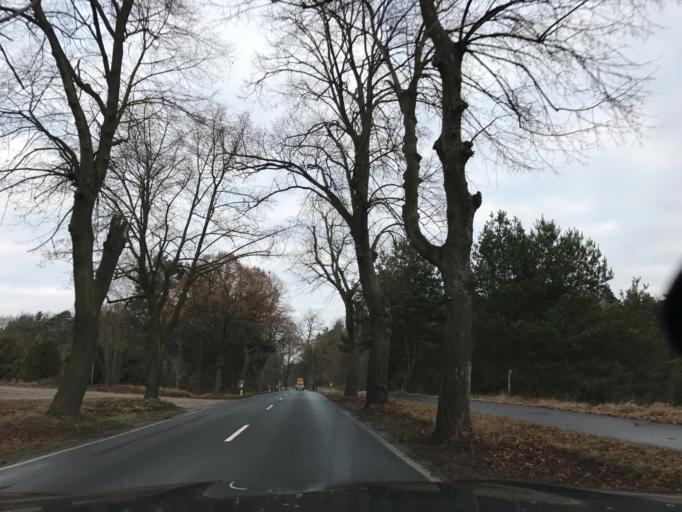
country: DE
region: Brandenburg
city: Gross Kreutz
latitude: 52.3251
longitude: 12.7325
